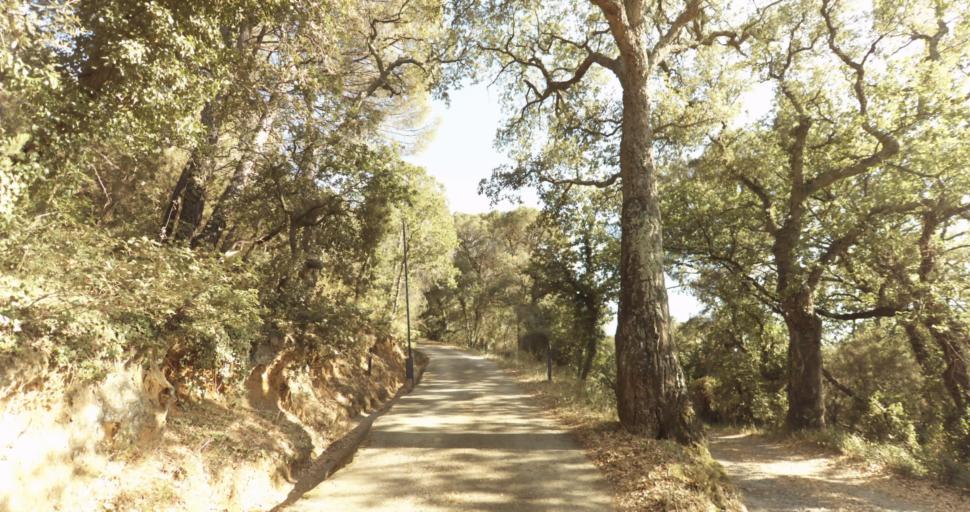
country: FR
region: Provence-Alpes-Cote d'Azur
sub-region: Departement du Var
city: Gassin
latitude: 43.2278
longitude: 6.5802
